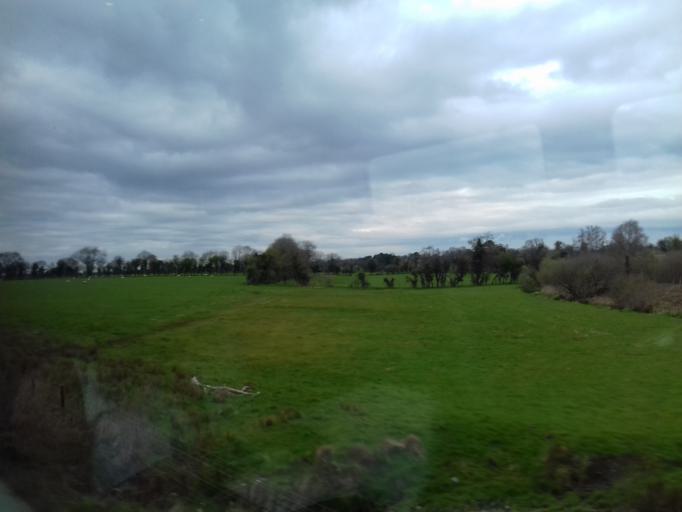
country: IE
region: Leinster
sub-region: An Longfort
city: Granard
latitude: 53.6651
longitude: -7.4725
